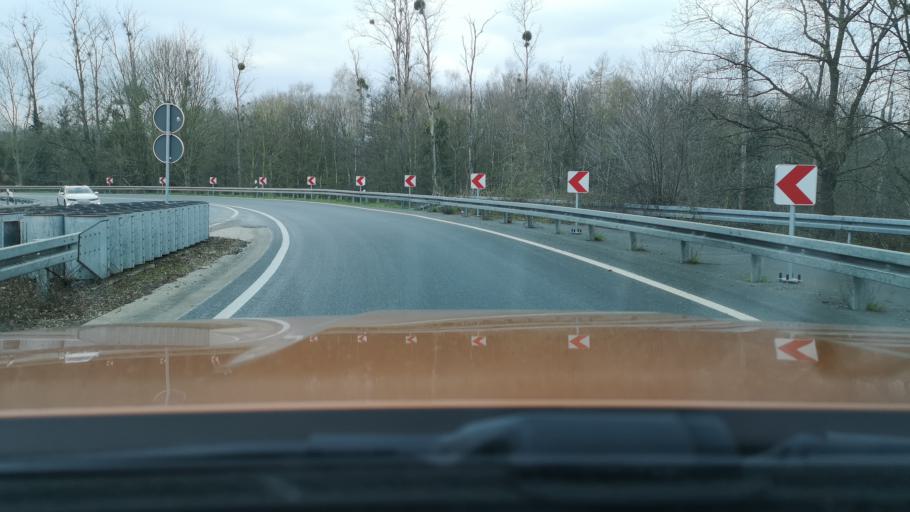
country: DE
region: Lower Saxony
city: Nienstadt
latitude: 52.3072
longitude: 9.1872
